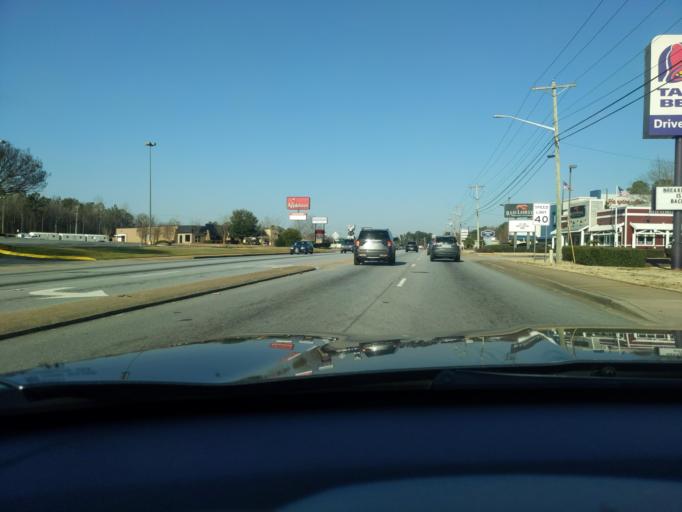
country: US
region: South Carolina
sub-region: Greenwood County
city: Greenwood
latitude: 34.2165
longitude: -82.1578
